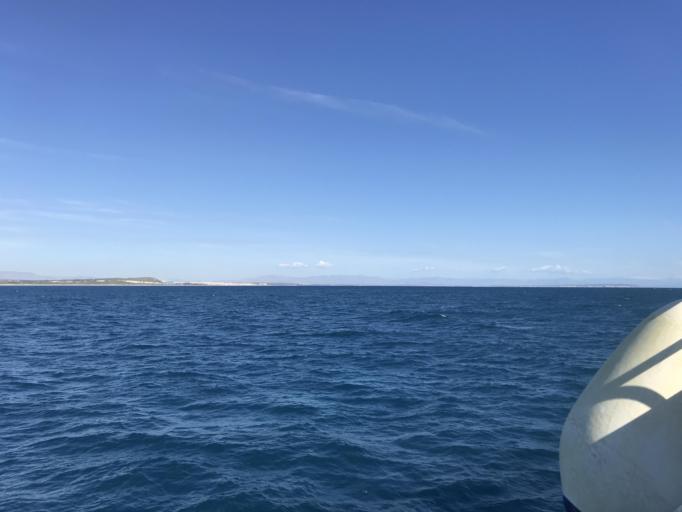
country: ES
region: Valencia
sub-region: Provincia de Alicante
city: Torrevieja
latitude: 38.0122
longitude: -0.6280
